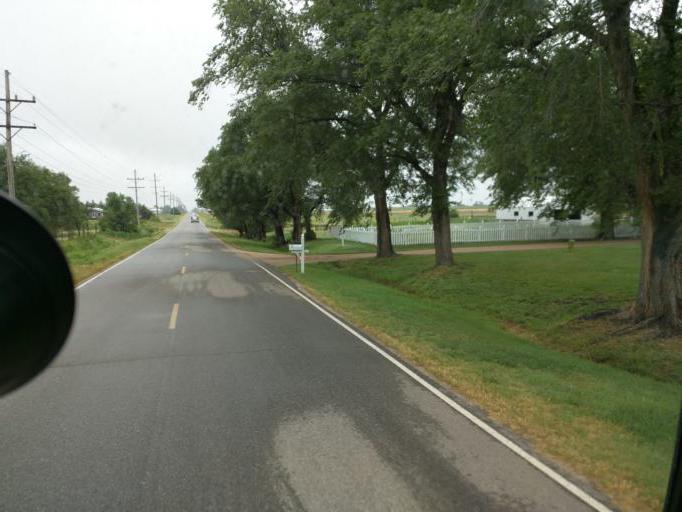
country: US
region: Kansas
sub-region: Reno County
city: Haven
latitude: 37.9316
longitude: -97.8852
